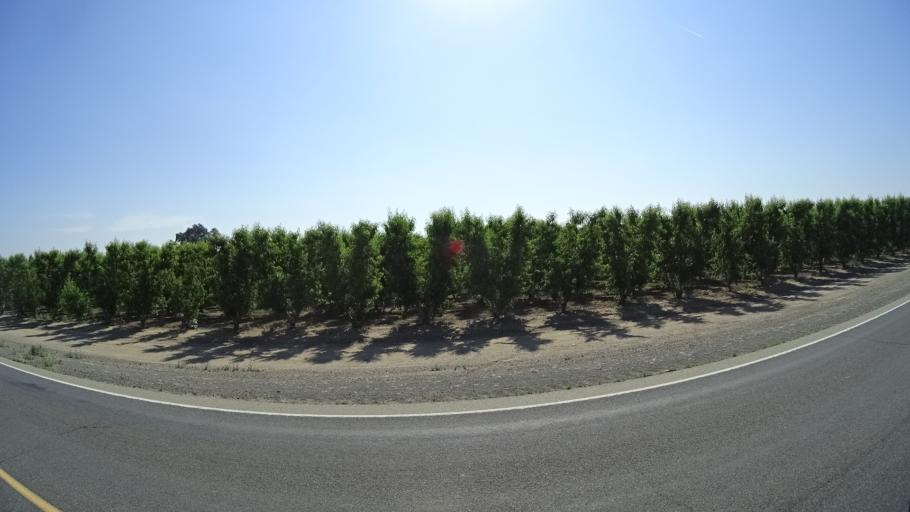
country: US
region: California
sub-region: Fresno County
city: Kingsburg
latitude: 36.4389
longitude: -119.5647
